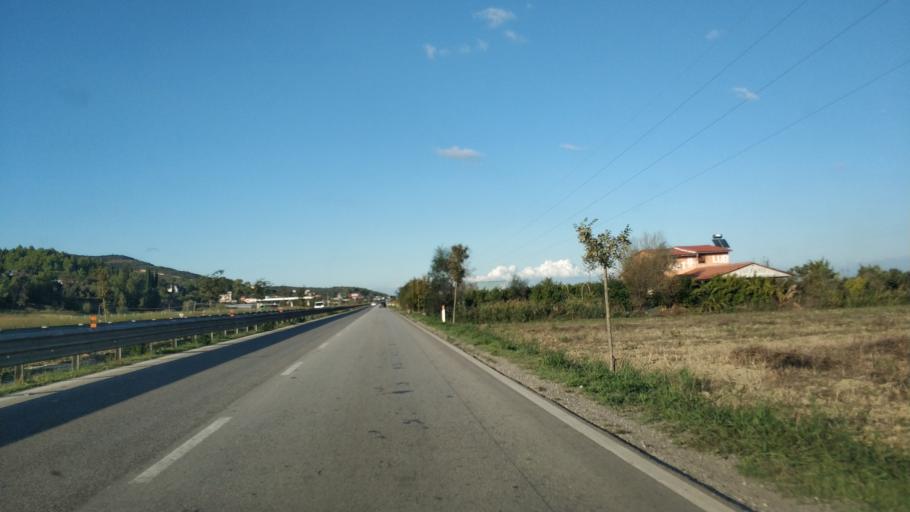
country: AL
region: Fier
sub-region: Rrethi i Fierit
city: Mbrostar-Ure
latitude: 40.7809
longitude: 19.5955
